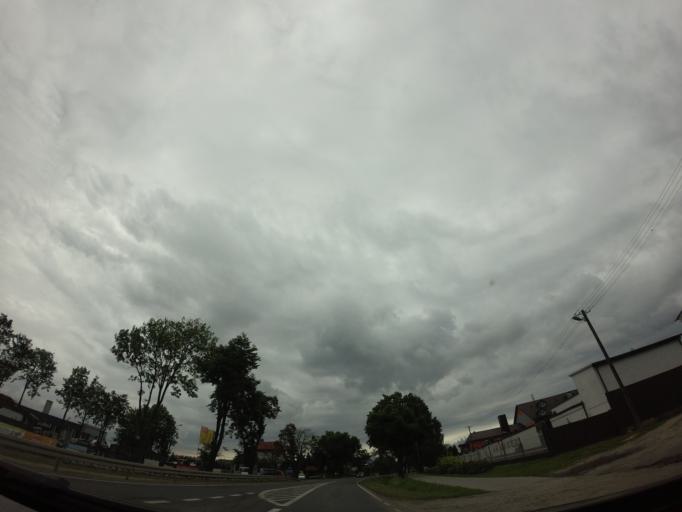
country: PL
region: Masovian Voivodeship
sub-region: Powiat ciechanowski
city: Glinojeck
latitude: 52.8194
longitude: 20.2918
